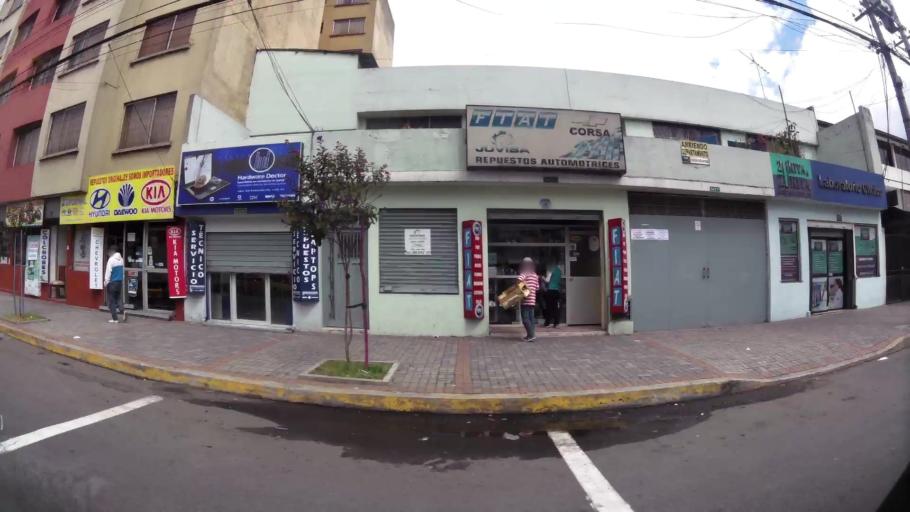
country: EC
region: Pichincha
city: Quito
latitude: -0.2485
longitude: -78.5275
